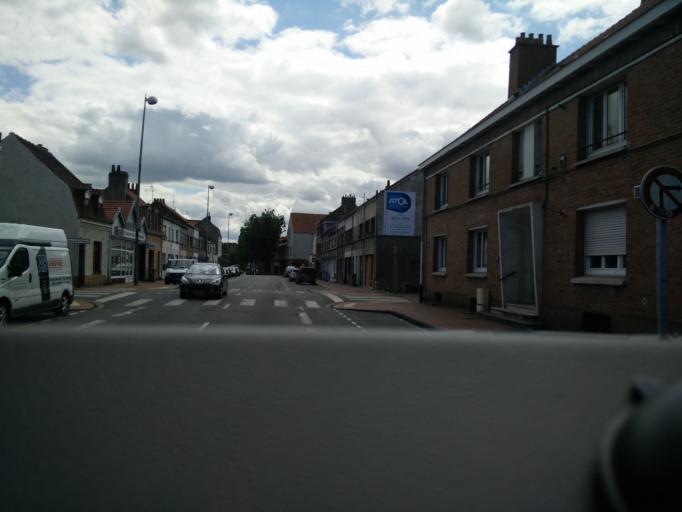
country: FR
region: Nord-Pas-de-Calais
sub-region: Departement du Nord
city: Coudekerque-Branche
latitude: 51.0428
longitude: 2.4045
